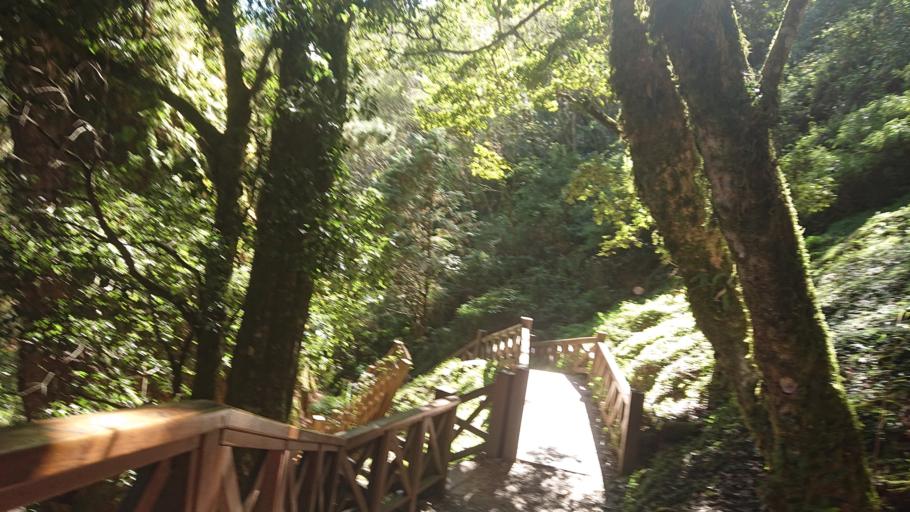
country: TW
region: Taiwan
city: Lugu
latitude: 23.4819
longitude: 120.8553
